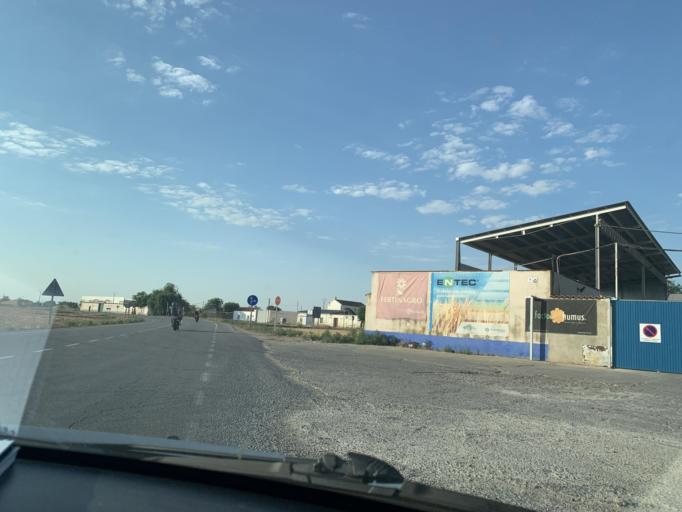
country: ES
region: Castille-La Mancha
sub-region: Provincia de Ciudad Real
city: Argamasilla de Alba
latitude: 39.1692
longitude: -3.2293
